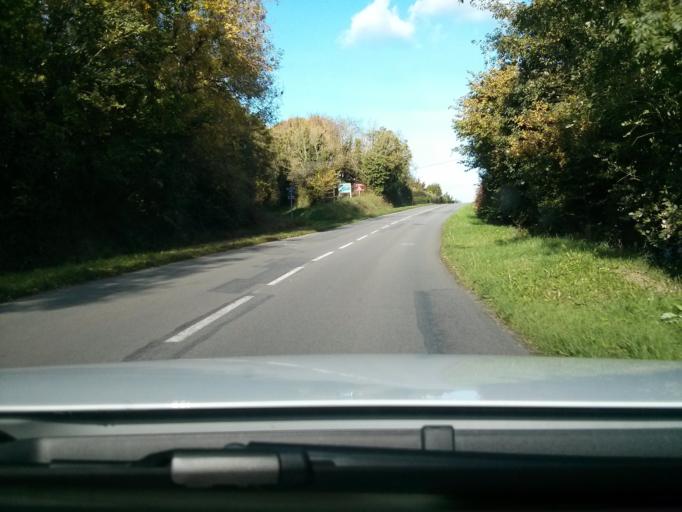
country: FR
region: Brittany
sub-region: Departement des Cotes-d'Armor
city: Crehen
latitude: 48.5828
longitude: -2.1893
